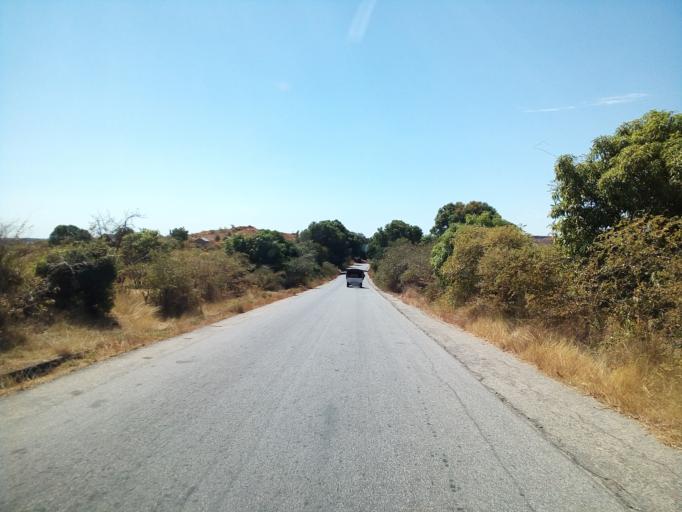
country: MG
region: Betsiboka
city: Maevatanana
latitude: -16.9169
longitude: 46.8691
